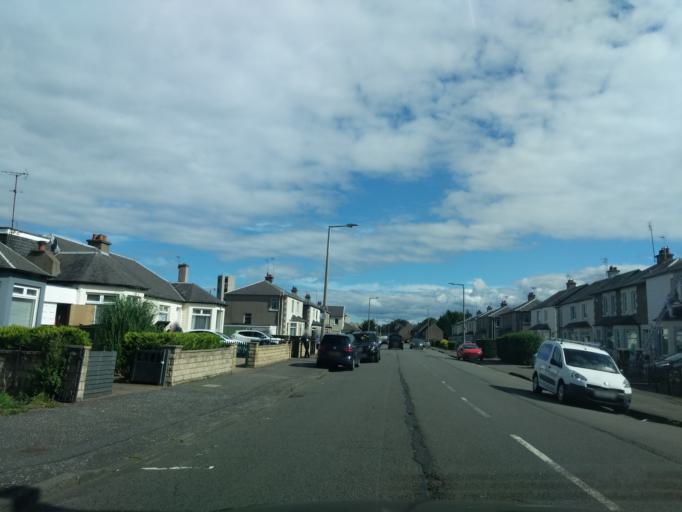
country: GB
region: Scotland
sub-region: West Lothian
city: Seafield
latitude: 55.9576
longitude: -3.1532
